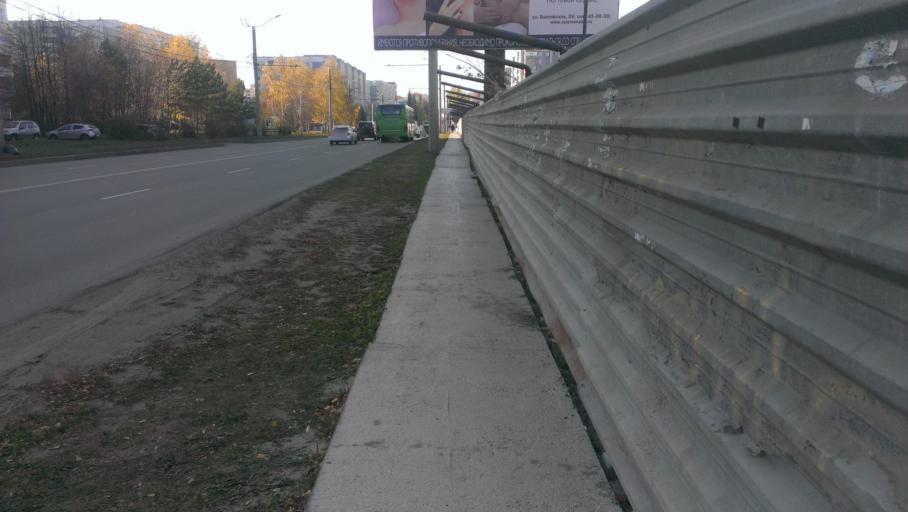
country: RU
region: Altai Krai
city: Novosilikatnyy
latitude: 53.3351
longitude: 83.6826
